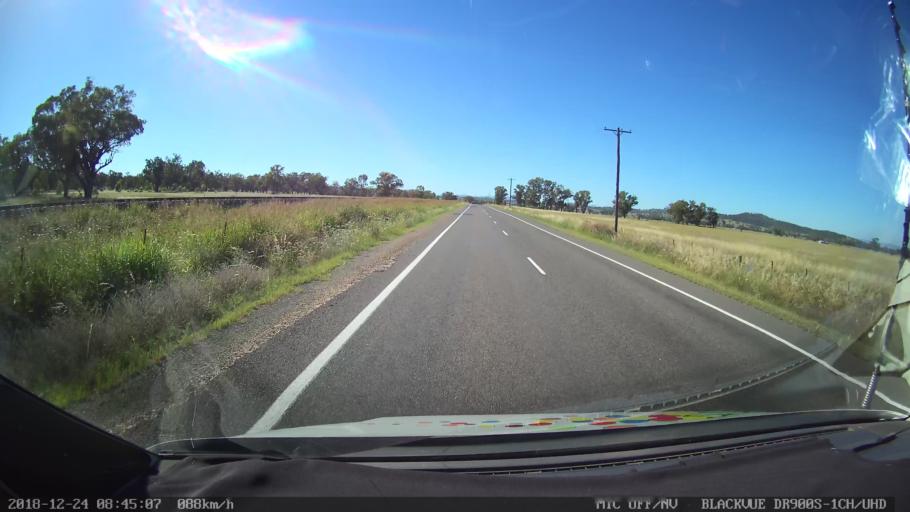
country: AU
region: New South Wales
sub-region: Liverpool Plains
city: Quirindi
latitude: -31.4108
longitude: 150.6509
